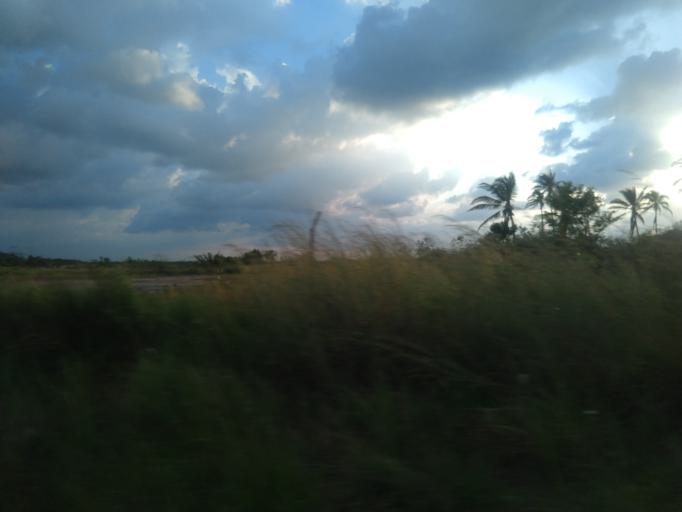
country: MZ
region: Sofala
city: Beira
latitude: -19.6730
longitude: 35.1256
